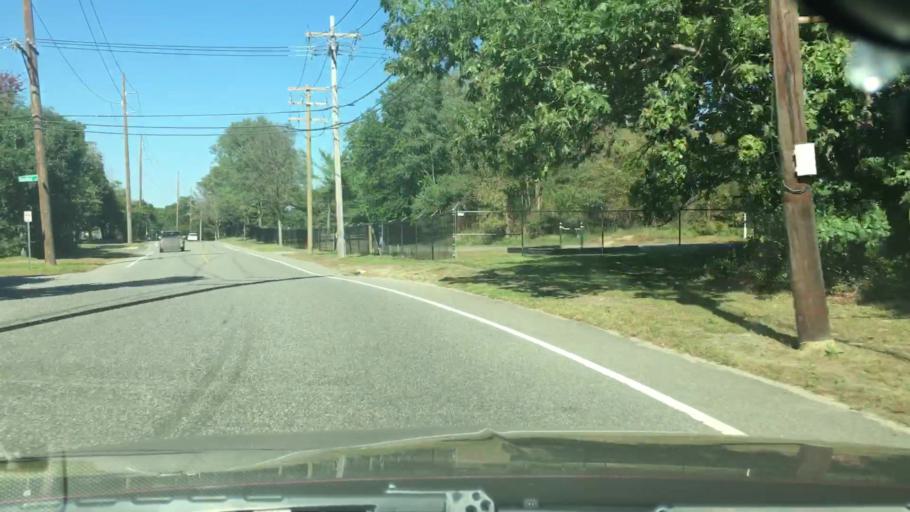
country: US
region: New York
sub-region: Suffolk County
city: Holtsville
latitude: 40.7988
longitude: -73.0381
